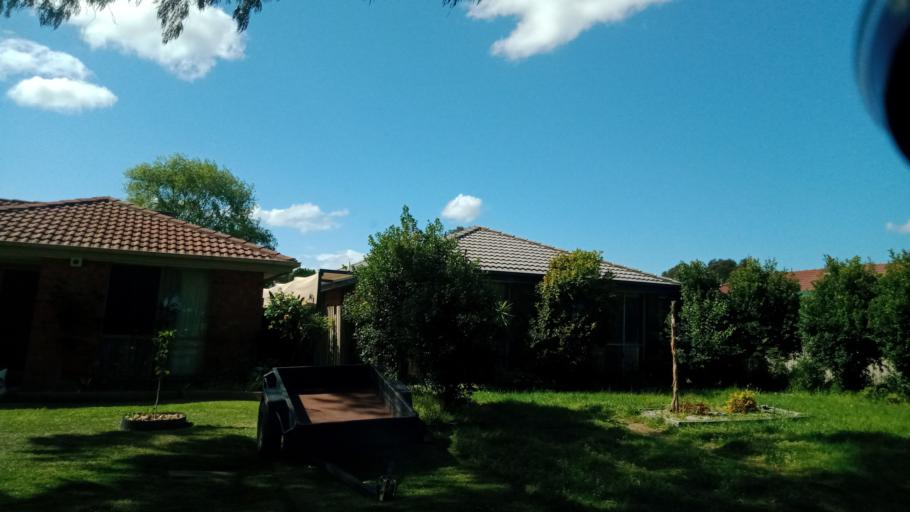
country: AU
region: Victoria
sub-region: Casey
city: Cranbourne West
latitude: -38.0973
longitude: 145.2591
